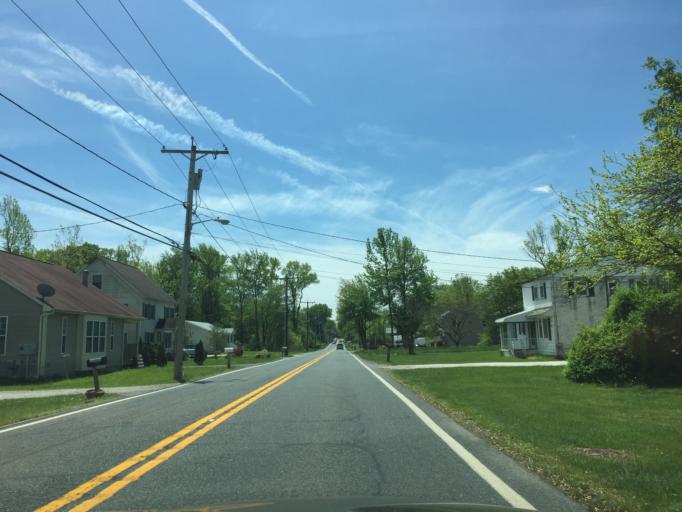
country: US
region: Maryland
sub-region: Baltimore County
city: Bowleys Quarters
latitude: 39.3564
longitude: -76.3737
